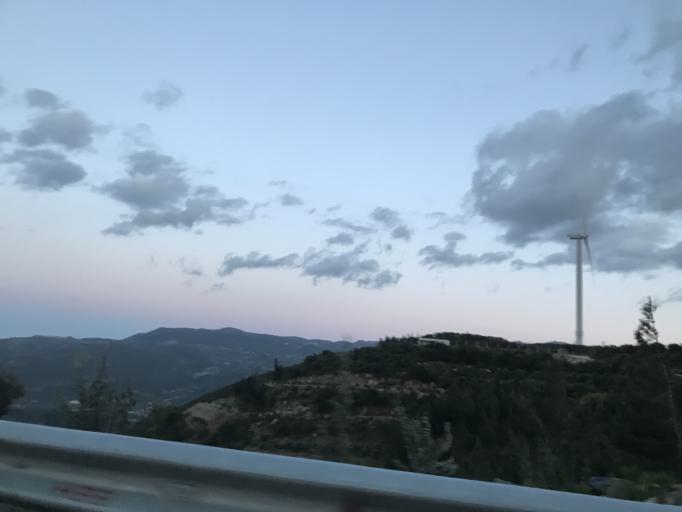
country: TR
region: Hatay
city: Uzunbag
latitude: 36.1072
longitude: 36.0431
